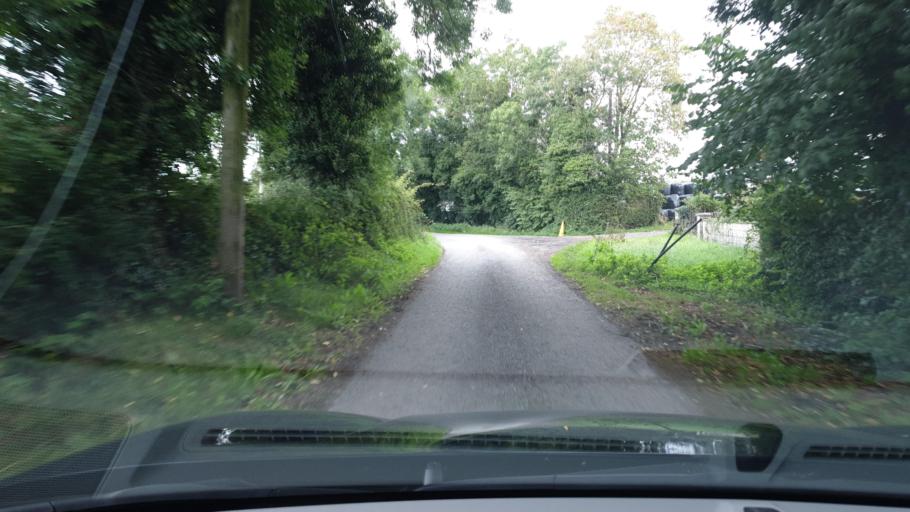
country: IE
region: Leinster
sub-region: Kildare
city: Maynooth
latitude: 53.3371
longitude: -6.6387
